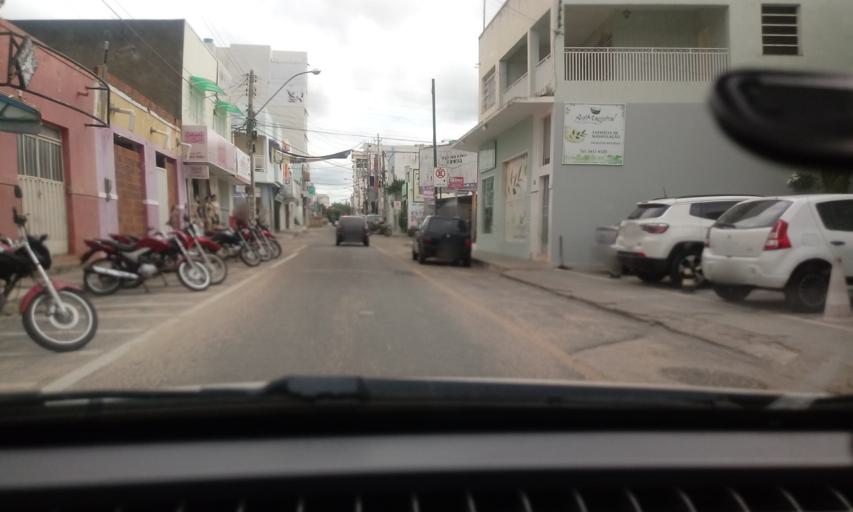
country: BR
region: Bahia
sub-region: Guanambi
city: Guanambi
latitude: -14.2251
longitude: -42.7798
